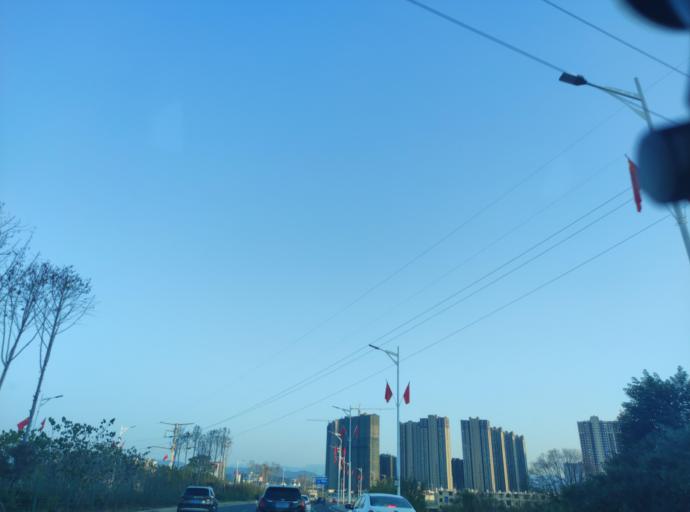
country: CN
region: Jiangxi Sheng
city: Pingxiang
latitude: 27.6416
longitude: 113.8279
